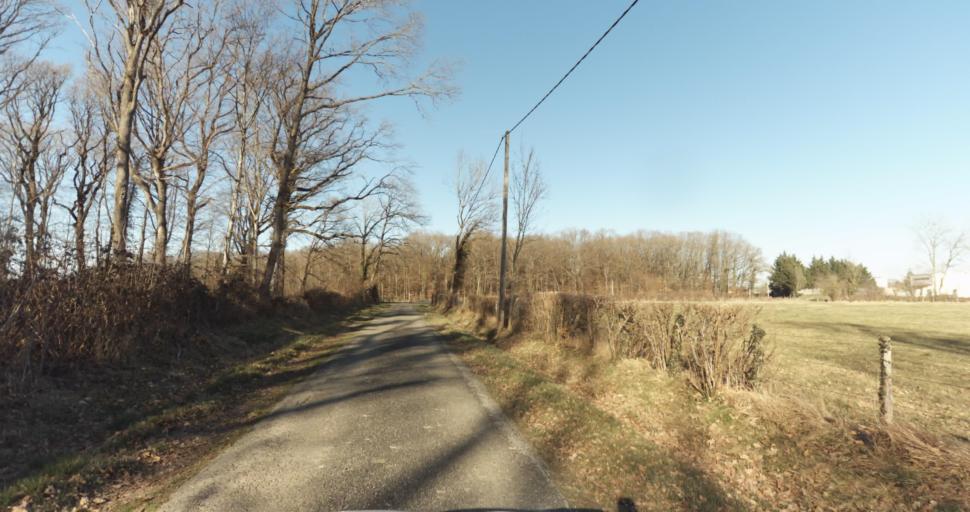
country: FR
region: Franche-Comte
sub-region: Departement du Jura
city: Montmorot
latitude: 46.6898
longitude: 5.4992
